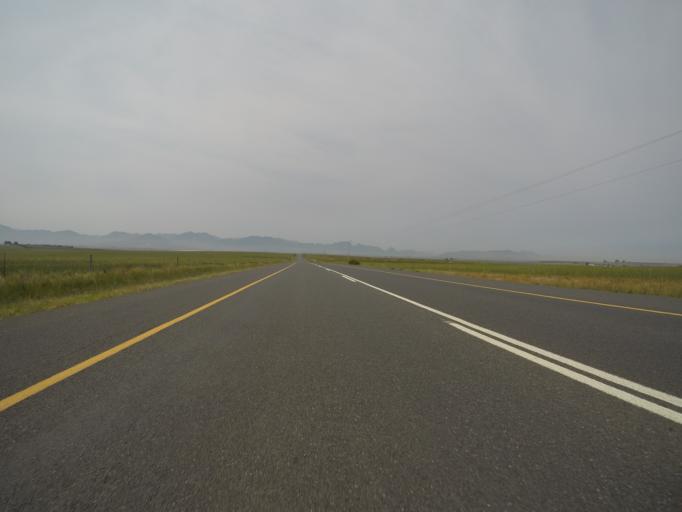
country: ZA
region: Western Cape
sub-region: Cape Winelands District Municipality
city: Noorder-Paarl
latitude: -33.5641
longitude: 18.8830
